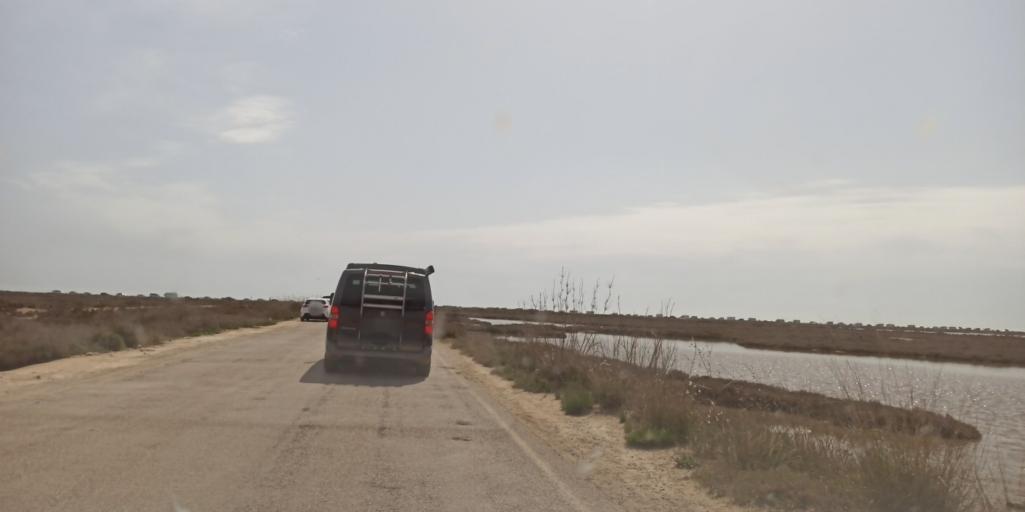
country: ES
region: Catalonia
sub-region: Provincia de Tarragona
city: Deltebre
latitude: 40.6386
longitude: 0.7431
